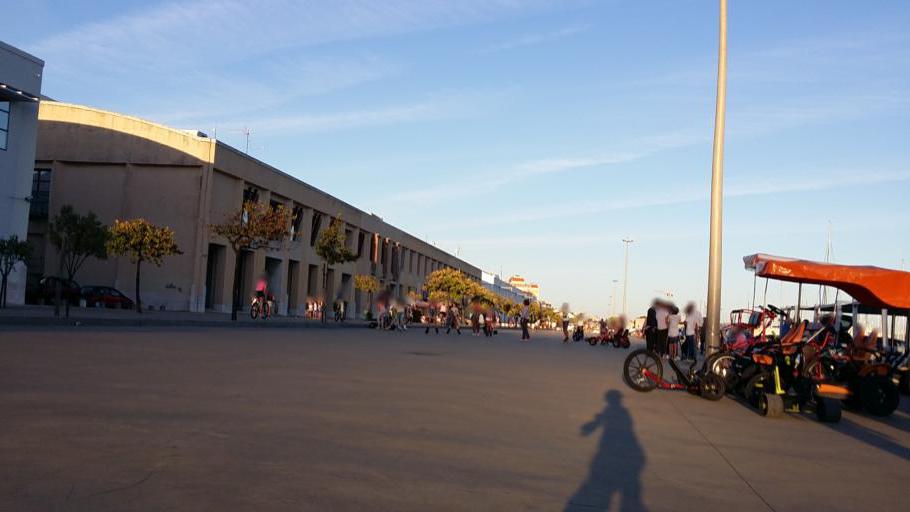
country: PT
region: Setubal
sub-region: Almada
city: Almada
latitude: 38.7019
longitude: -9.1716
